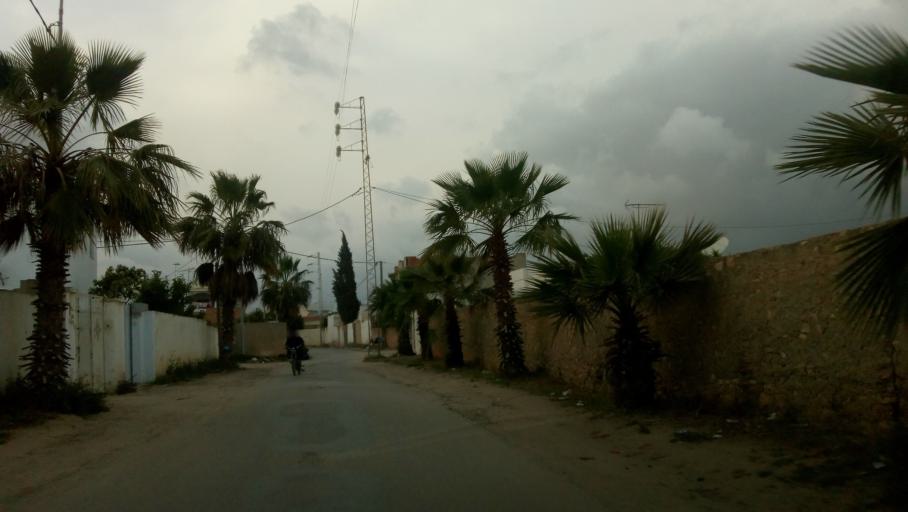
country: TN
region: Safaqis
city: Sfax
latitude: 34.7683
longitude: 10.7019
